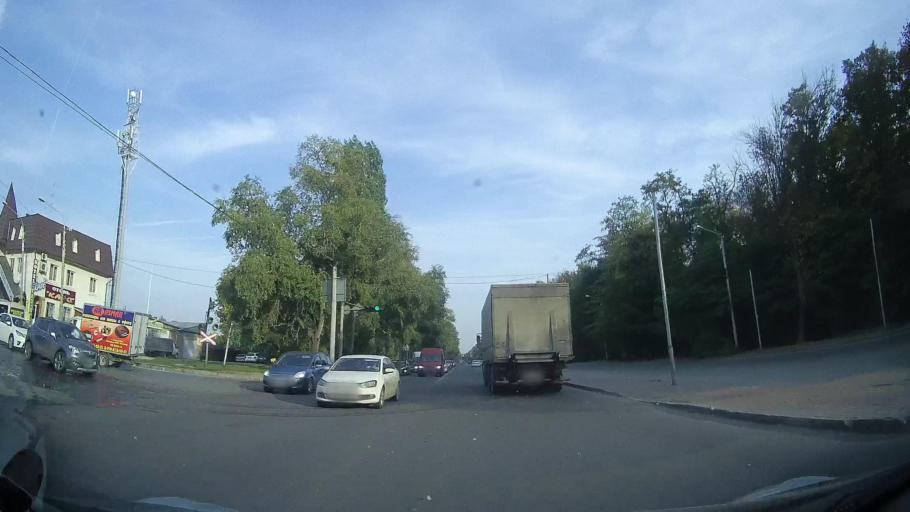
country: RU
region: Rostov
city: Imeni Chkalova
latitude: 47.2774
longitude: 39.8022
